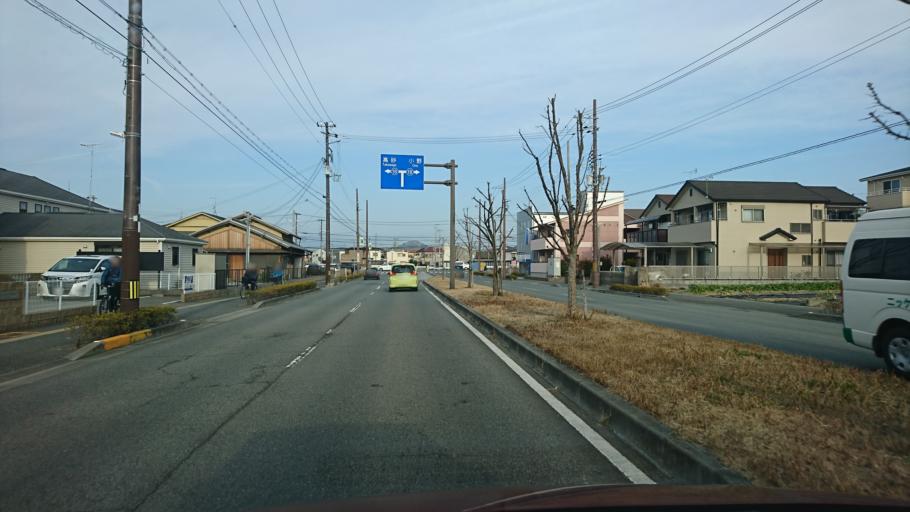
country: JP
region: Hyogo
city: Kakogawacho-honmachi
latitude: 34.7696
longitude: 134.8417
